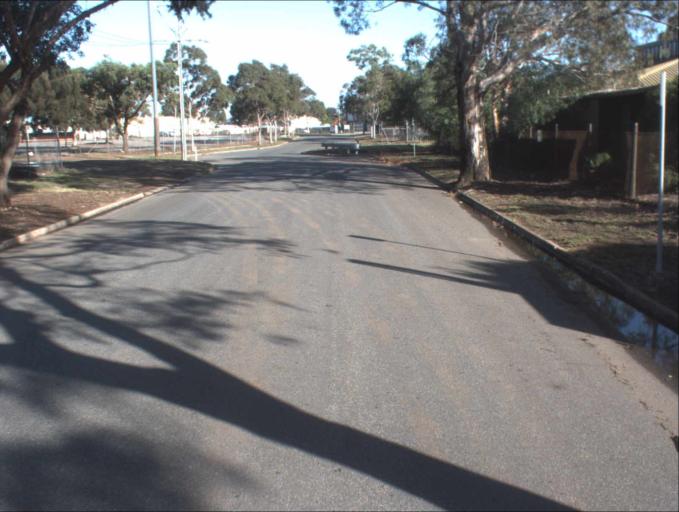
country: AU
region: South Australia
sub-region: Charles Sturt
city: Woodville North
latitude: -34.8461
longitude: 138.5440
